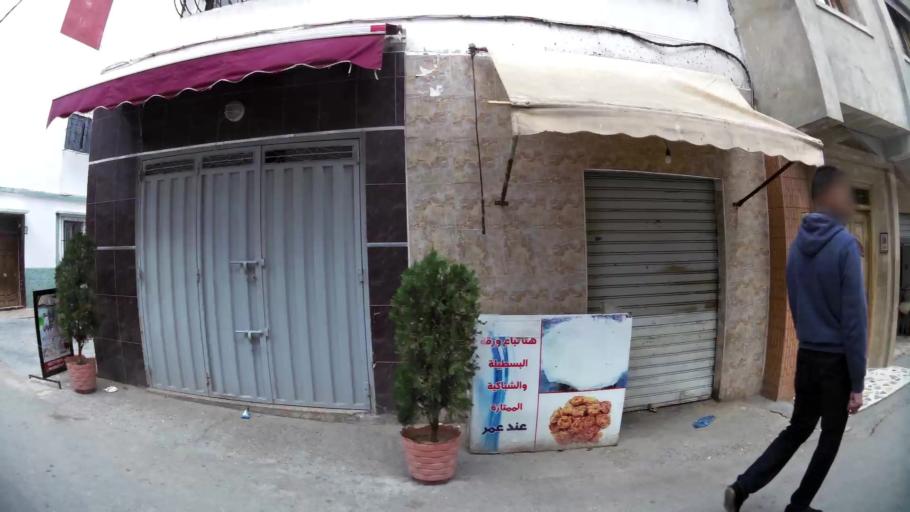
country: MA
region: Tanger-Tetouan
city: Tetouan
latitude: 35.5760
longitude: -5.3615
